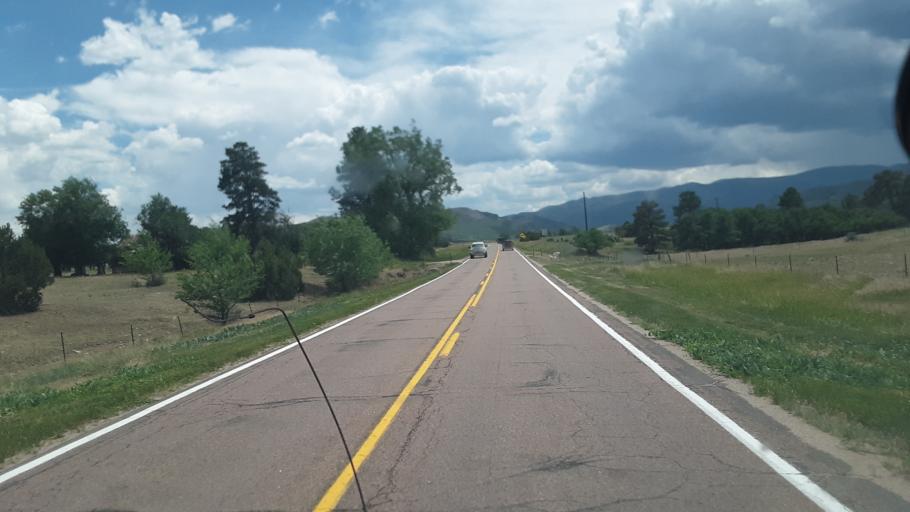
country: US
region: Colorado
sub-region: Fremont County
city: Florence
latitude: 38.2476
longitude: -105.0904
